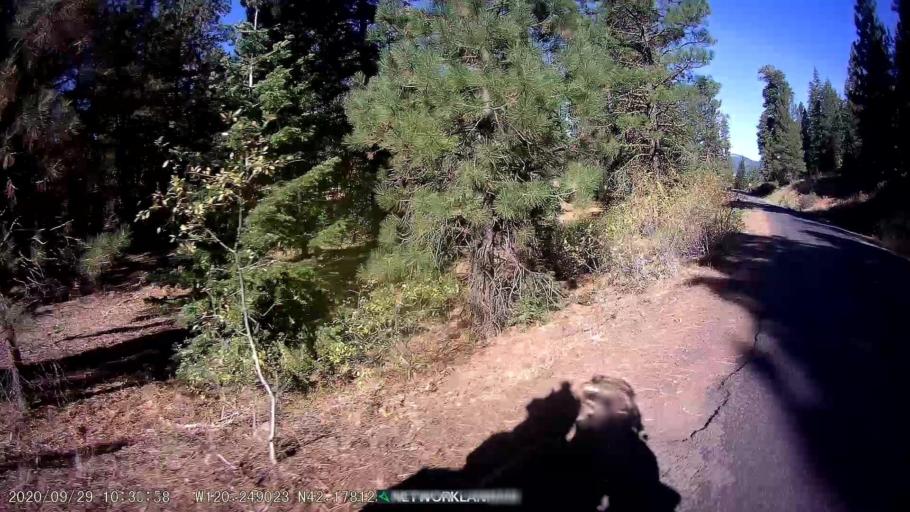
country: US
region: Oregon
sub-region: Lake County
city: Lakeview
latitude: 42.1782
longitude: -120.2490
